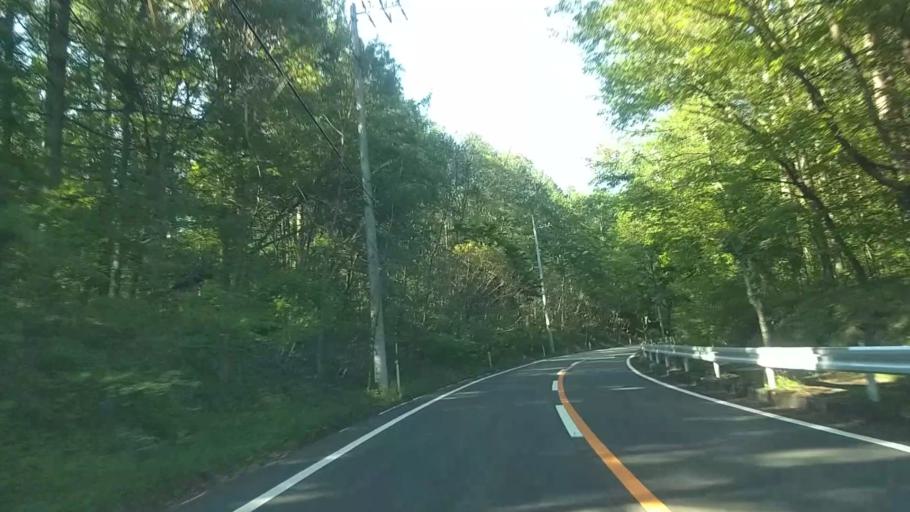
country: JP
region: Nagano
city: Chino
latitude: 35.8968
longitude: 138.3256
